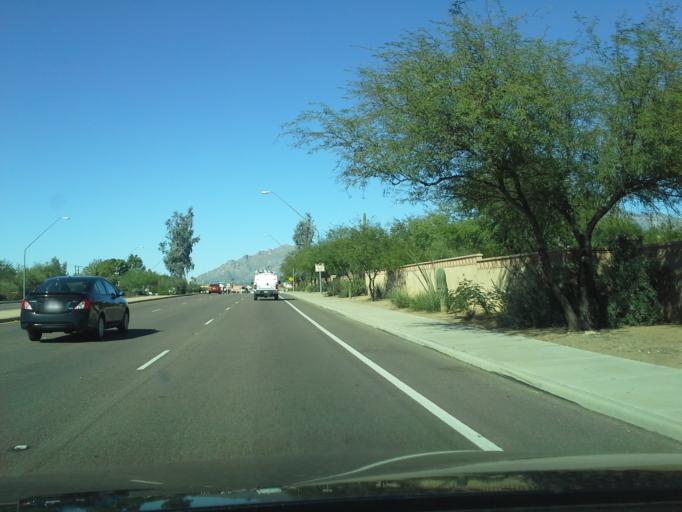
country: US
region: Arizona
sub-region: Pima County
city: Tucson
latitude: 32.2470
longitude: -110.9441
